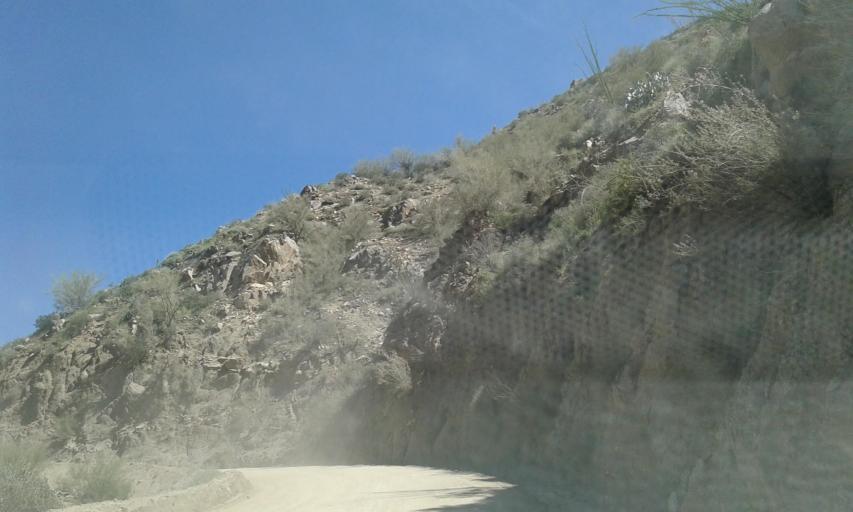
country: US
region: Arizona
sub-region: Gila County
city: Tonto Basin
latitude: 33.6558
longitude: -111.1828
